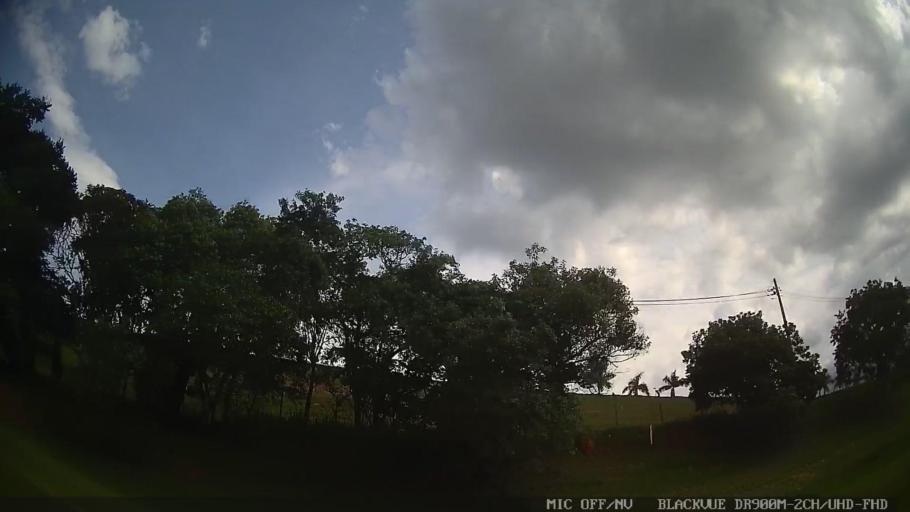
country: BR
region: Sao Paulo
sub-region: Itatiba
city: Itatiba
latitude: -23.0443
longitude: -46.8586
